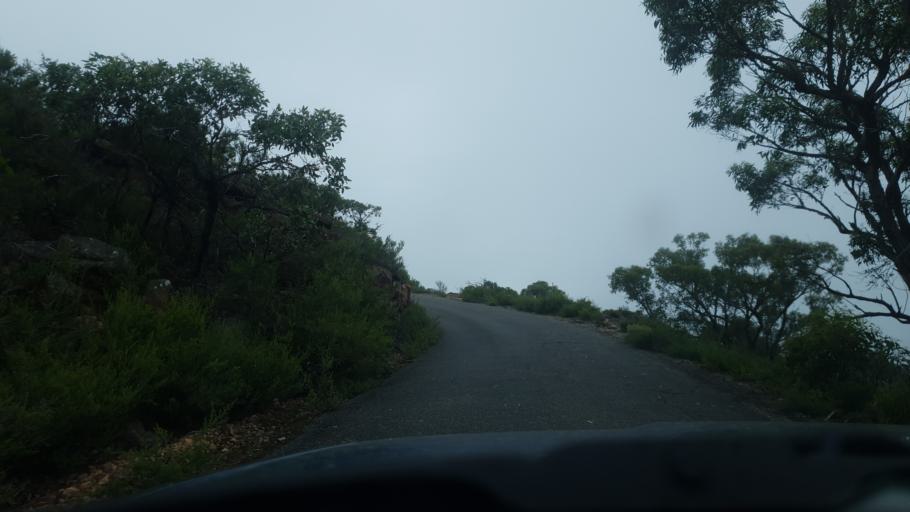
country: AU
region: Victoria
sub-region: Northern Grampians
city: Stawell
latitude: -37.2722
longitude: 142.5813
